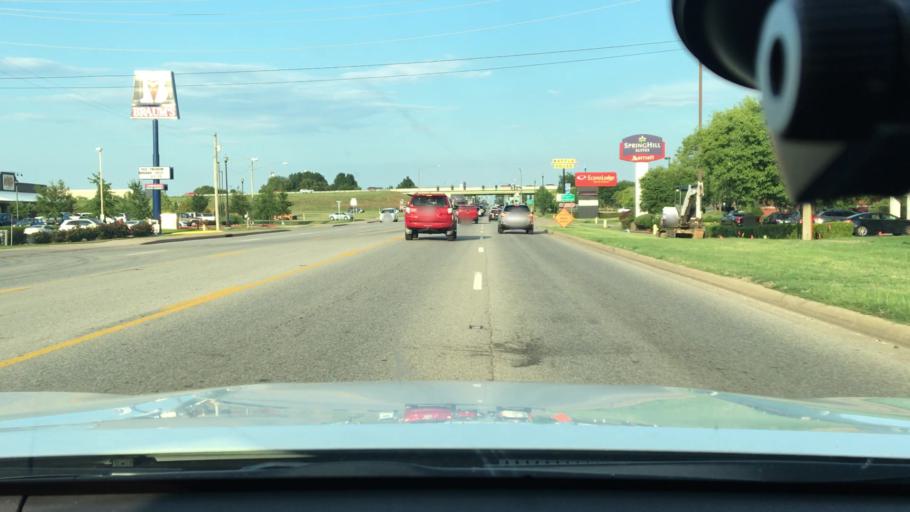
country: US
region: Arkansas
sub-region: Benton County
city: Bentonville
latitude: 36.3351
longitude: -94.1872
